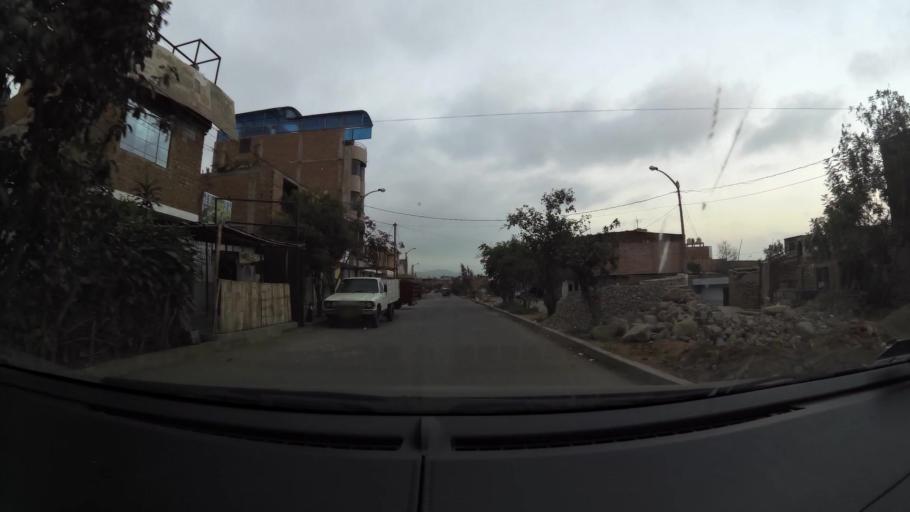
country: PE
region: La Libertad
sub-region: Provincia de Trujillo
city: El Porvenir
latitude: -8.0816
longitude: -79.0191
